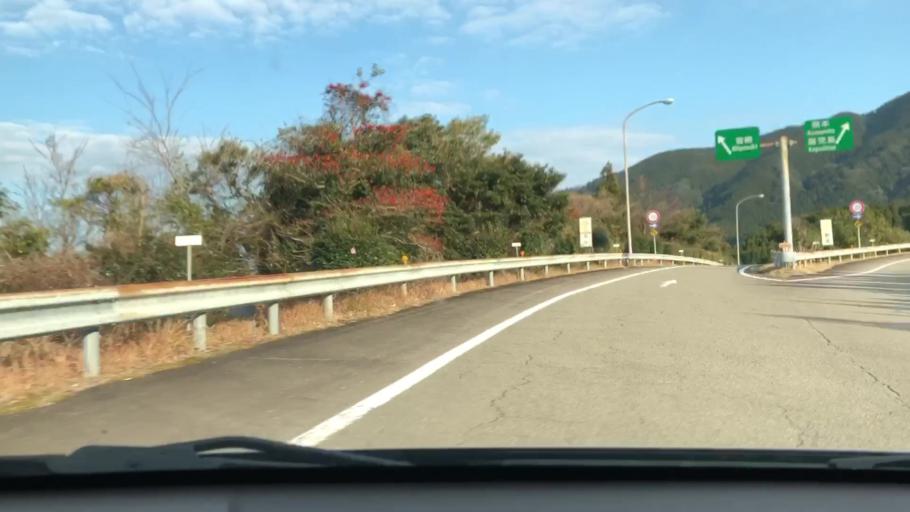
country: JP
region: Miyazaki
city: Miyazaki-shi
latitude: 31.8222
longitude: 131.3015
